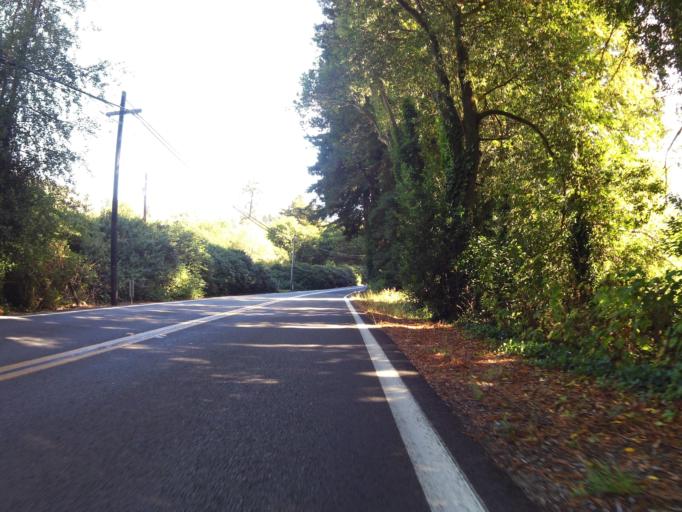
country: US
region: California
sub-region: Del Norte County
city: Bertsch-Oceanview
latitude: 41.8493
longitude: -124.1193
